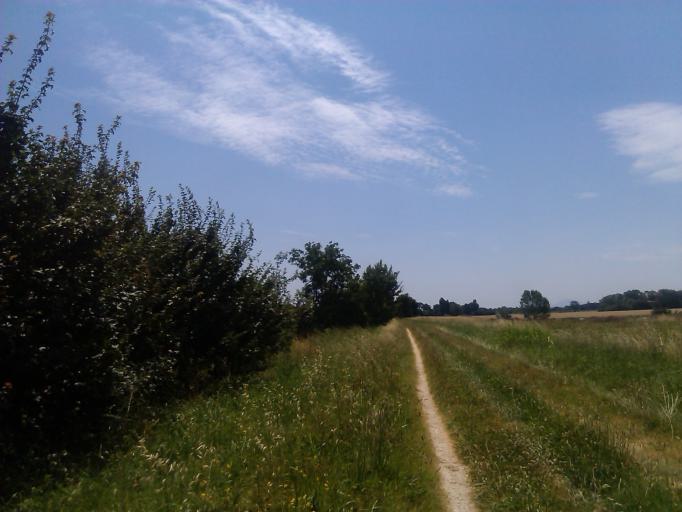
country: IT
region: Tuscany
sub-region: Province of Arezzo
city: Cesa
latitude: 43.3263
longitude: 11.8328
